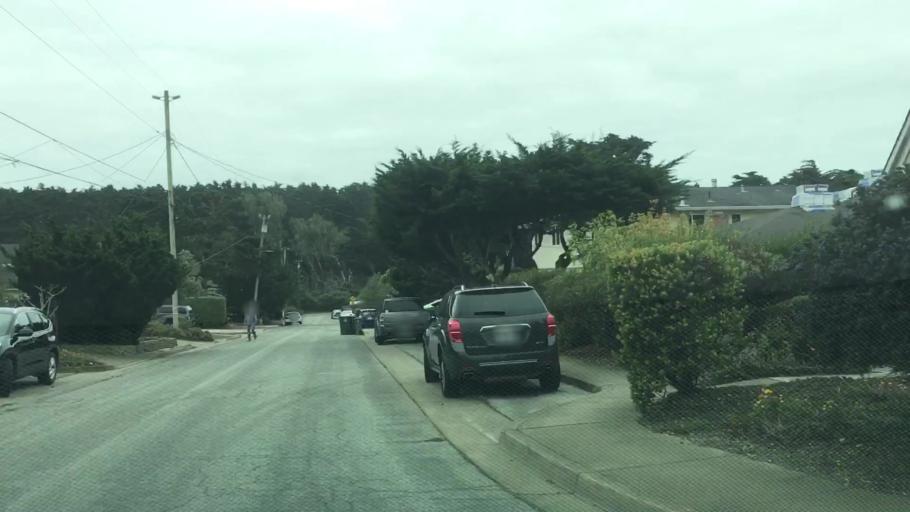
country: US
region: California
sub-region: San Mateo County
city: Moss Beach
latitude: 37.5250
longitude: -122.5141
